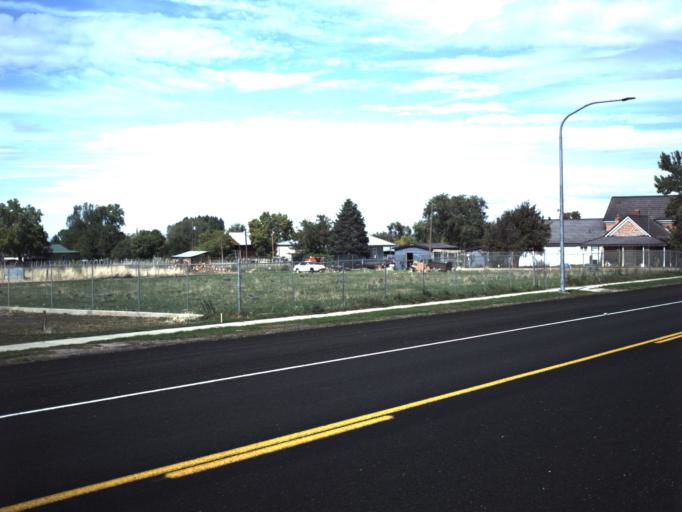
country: US
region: Utah
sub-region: Millard County
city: Fillmore
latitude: 38.7957
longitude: -112.4376
